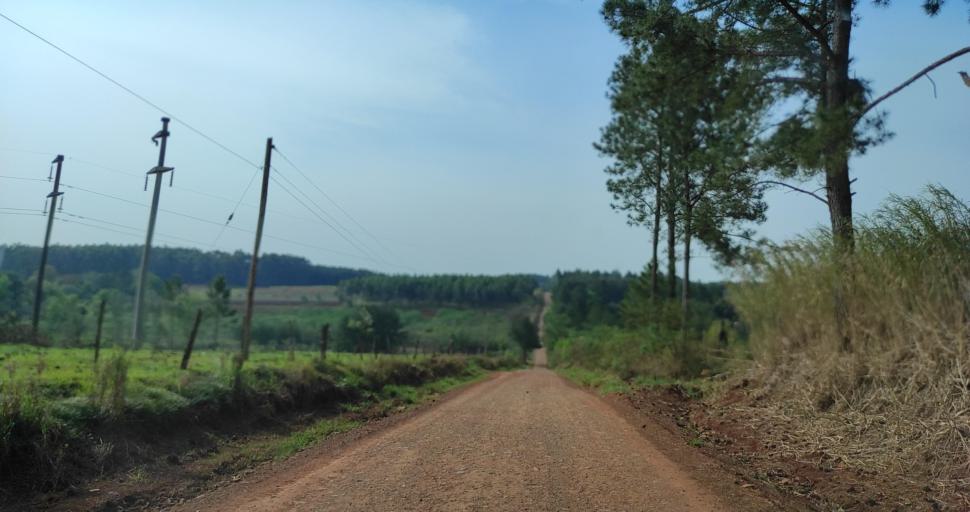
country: AR
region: Misiones
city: Garuhape
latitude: -26.8736
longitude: -55.0058
